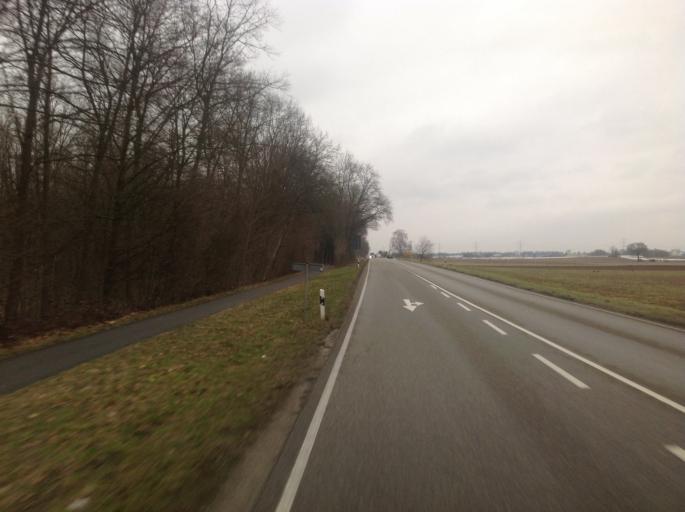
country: DE
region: Baden-Wuerttemberg
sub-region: Karlsruhe Region
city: Iffezheim
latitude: 48.8095
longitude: 8.1394
